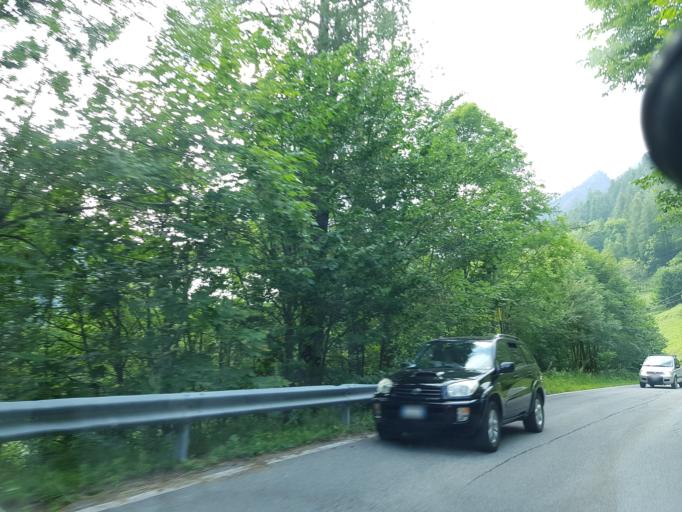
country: IT
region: Piedmont
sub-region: Provincia di Cuneo
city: Casteldelfino
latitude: 44.5856
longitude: 7.0530
